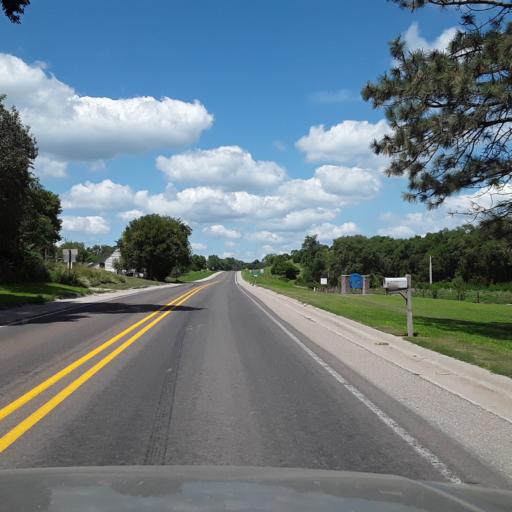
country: US
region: Nebraska
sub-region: Nance County
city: Genoa
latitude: 41.4528
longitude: -97.7254
